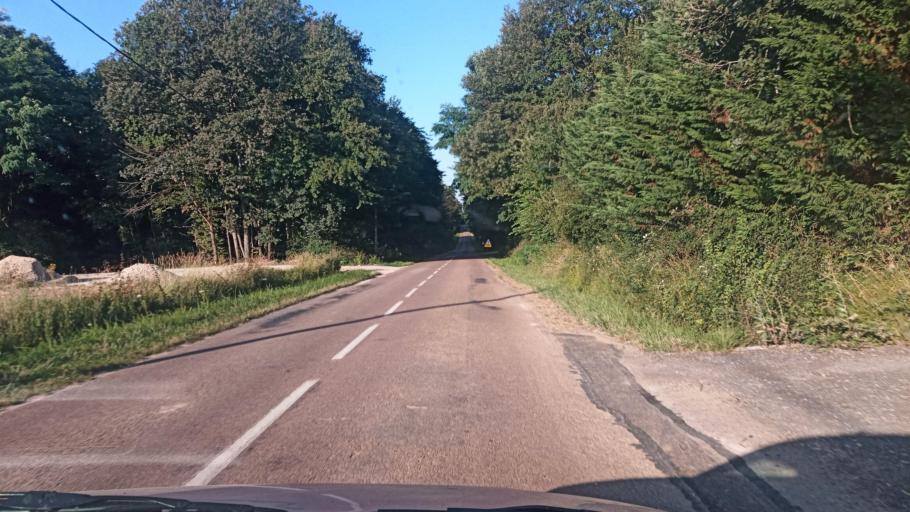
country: FR
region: Bourgogne
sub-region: Departement de l'Yonne
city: Pont-sur-Yonne
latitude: 48.2415
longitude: 3.1439
